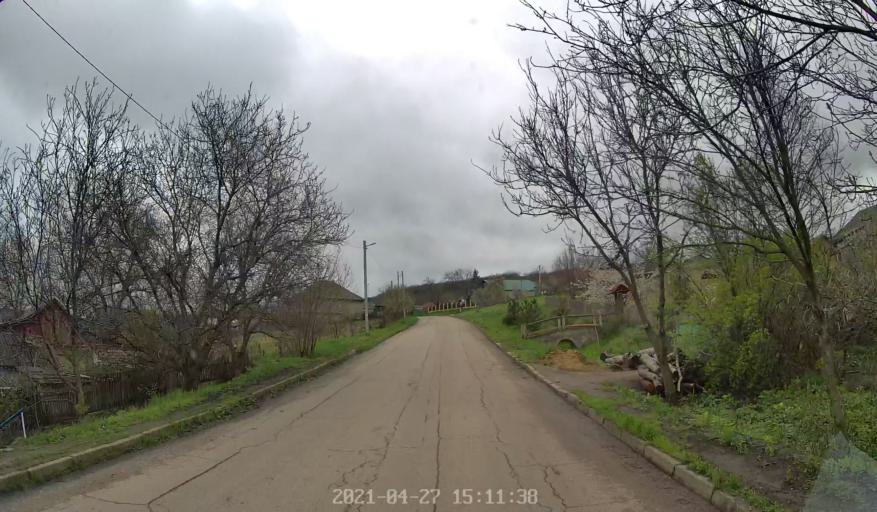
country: MD
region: Chisinau
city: Vadul lui Voda
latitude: 47.0305
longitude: 29.0258
